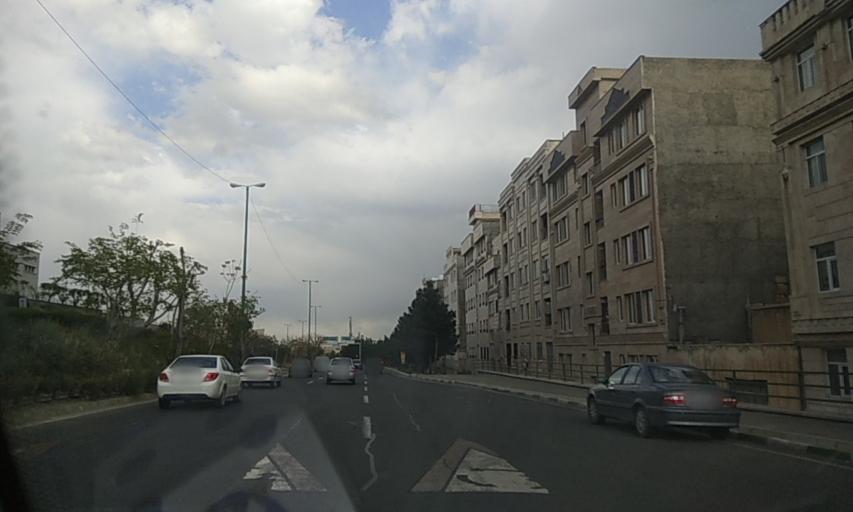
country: IR
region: Tehran
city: Tajrish
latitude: 35.7780
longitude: 51.3157
